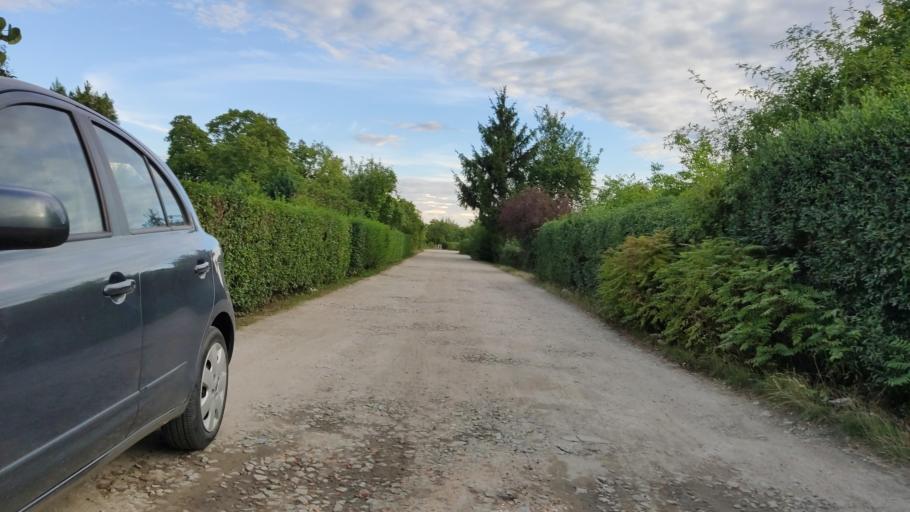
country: PL
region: Lower Silesian Voivodeship
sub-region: Powiat wroclawski
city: Wroclaw
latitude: 51.1011
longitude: 16.9799
